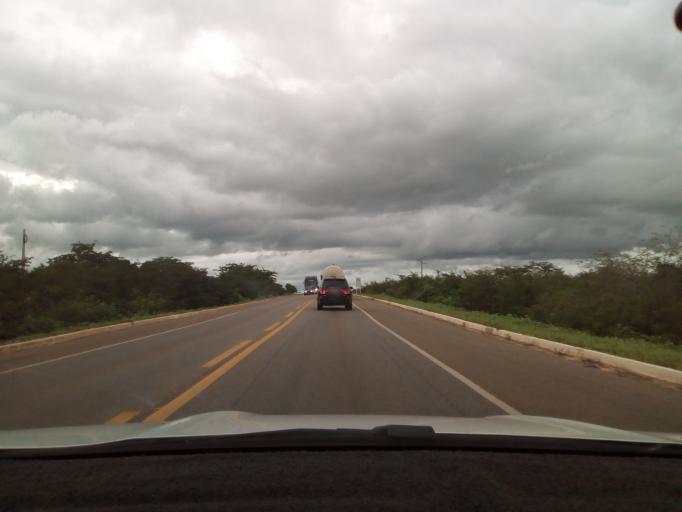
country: BR
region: Rio Grande do Norte
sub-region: Mossoro
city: Mossoro
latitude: -4.9484
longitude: -37.4038
